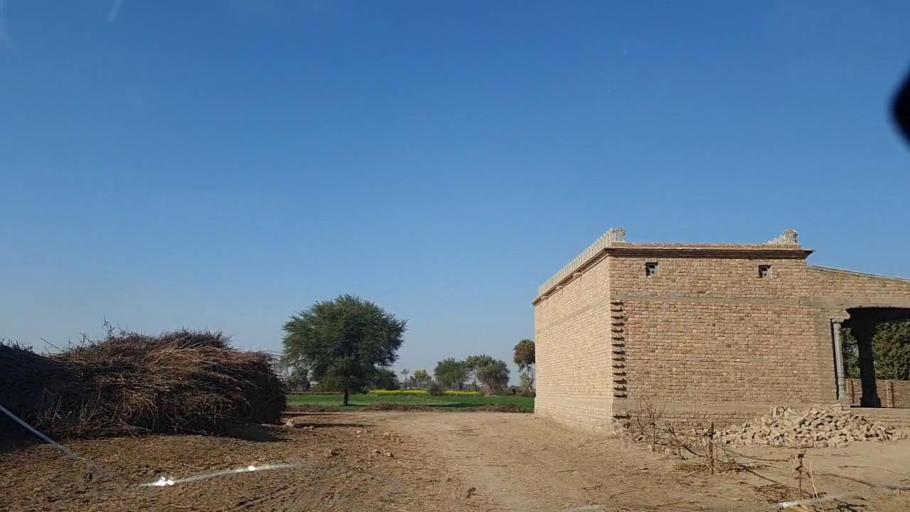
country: PK
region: Sindh
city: Khanpur
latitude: 27.7798
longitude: 69.3553
